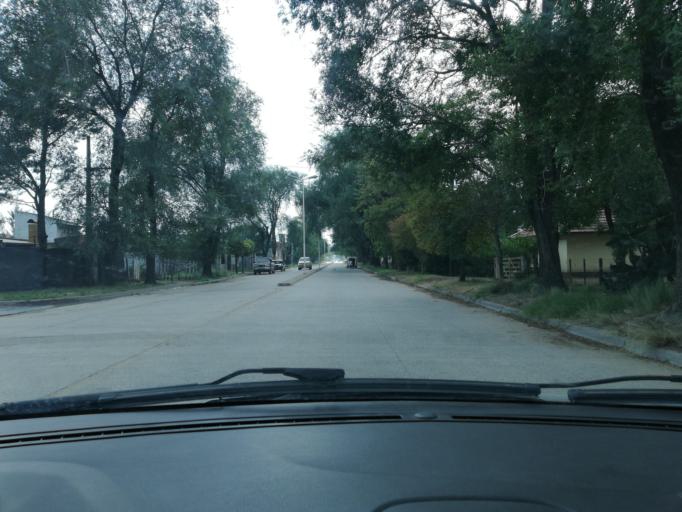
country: AR
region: Buenos Aires
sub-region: Partido de Balcarce
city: Balcarce
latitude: -37.8532
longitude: -58.2411
